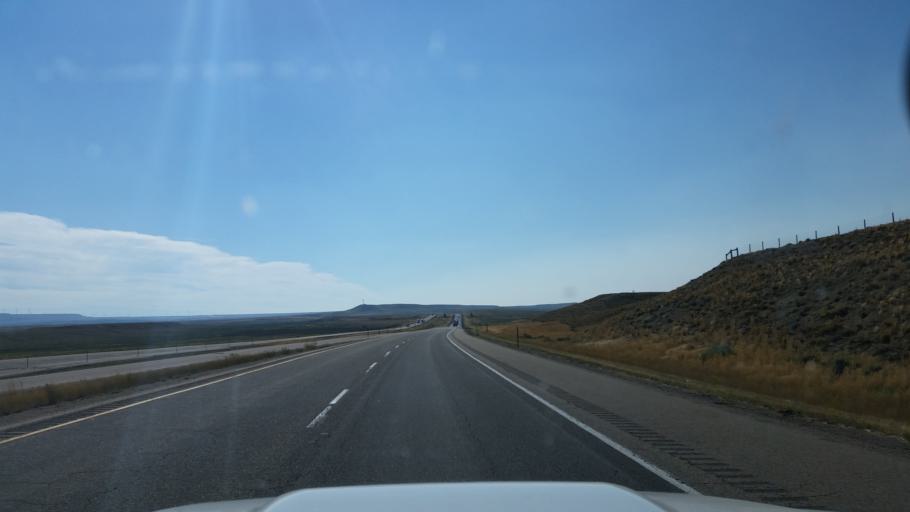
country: US
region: Wyoming
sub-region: Uinta County
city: Lyman
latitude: 41.3551
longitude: -110.3477
